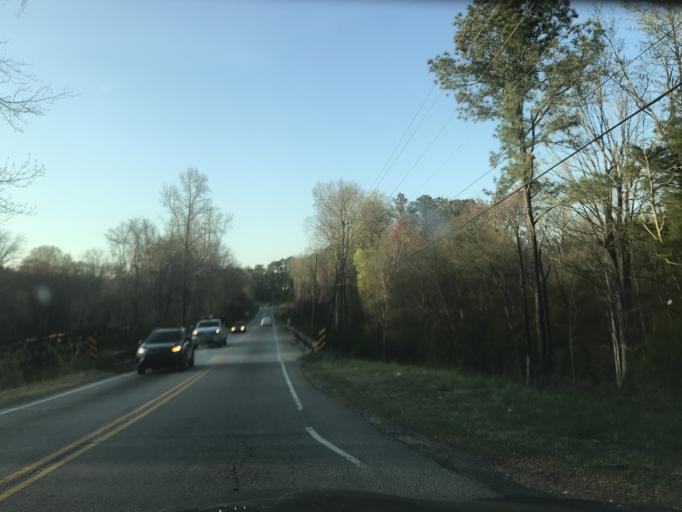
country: US
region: North Carolina
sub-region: Wake County
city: Knightdale
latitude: 35.7488
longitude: -78.5343
